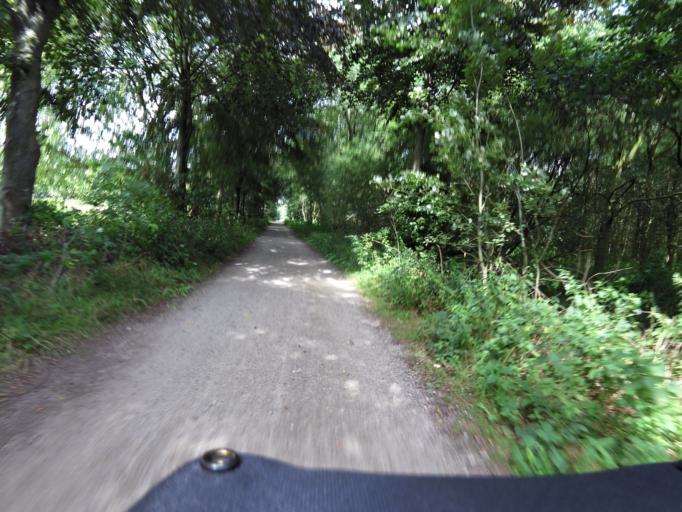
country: BE
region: Flanders
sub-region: Provincie Antwerpen
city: Baarle-Hertog
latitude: 51.4115
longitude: 4.8392
